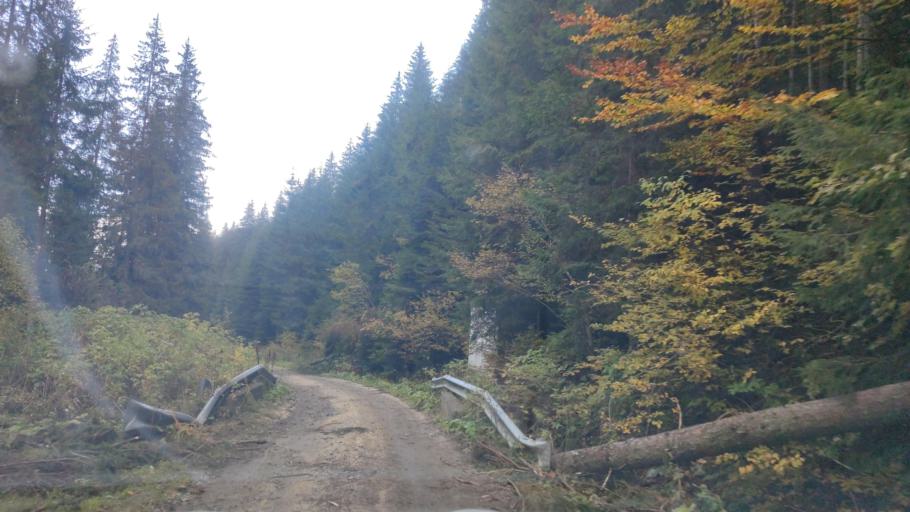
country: RO
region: Harghita
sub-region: Comuna Madaras
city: Madaras
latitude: 46.4720
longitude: 25.6432
